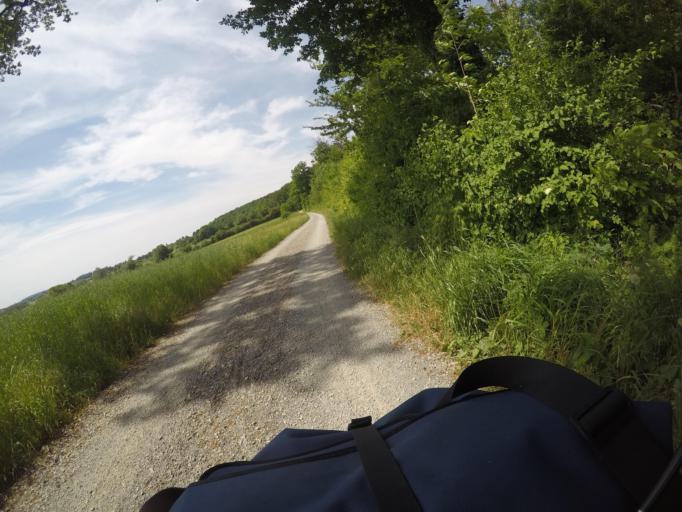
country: DE
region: Baden-Wuerttemberg
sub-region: Karlsruhe Region
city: Joehlingen
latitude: 48.9672
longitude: 8.5205
